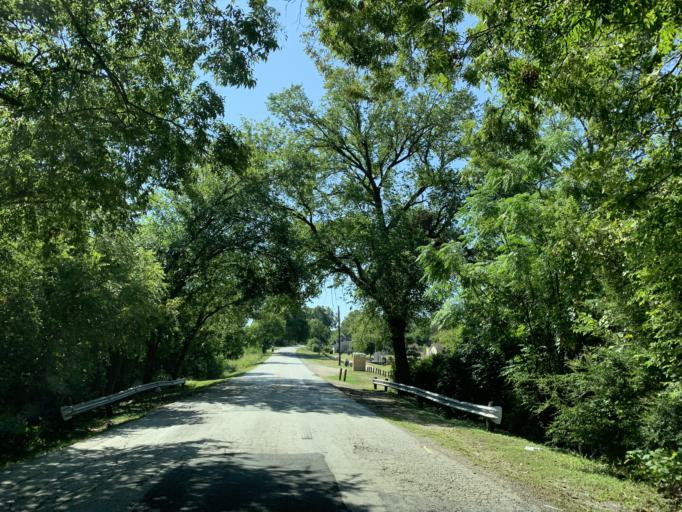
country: US
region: Texas
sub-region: Dallas County
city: Hutchins
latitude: 32.6738
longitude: -96.7474
